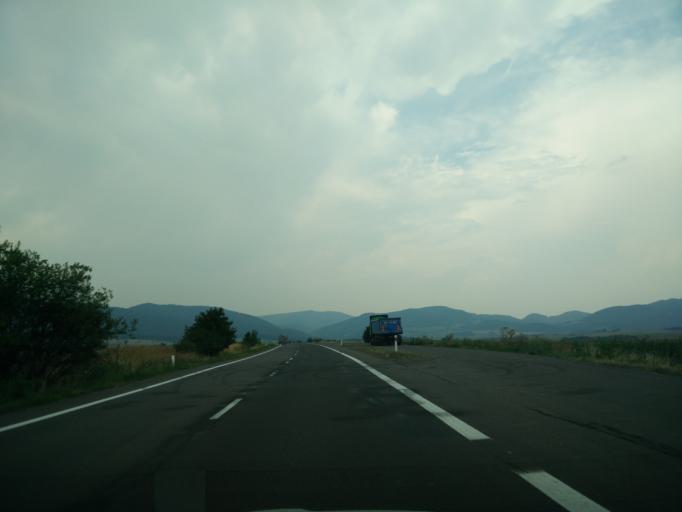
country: SK
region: Banskobystricky
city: Ziar nad Hronom
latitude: 48.6171
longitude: 18.8132
